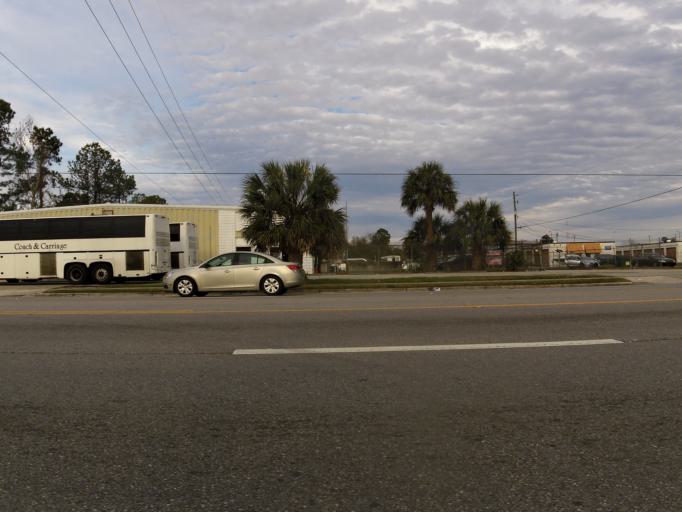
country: US
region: Florida
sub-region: Duval County
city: Jacksonville
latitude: 30.2593
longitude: -81.6192
